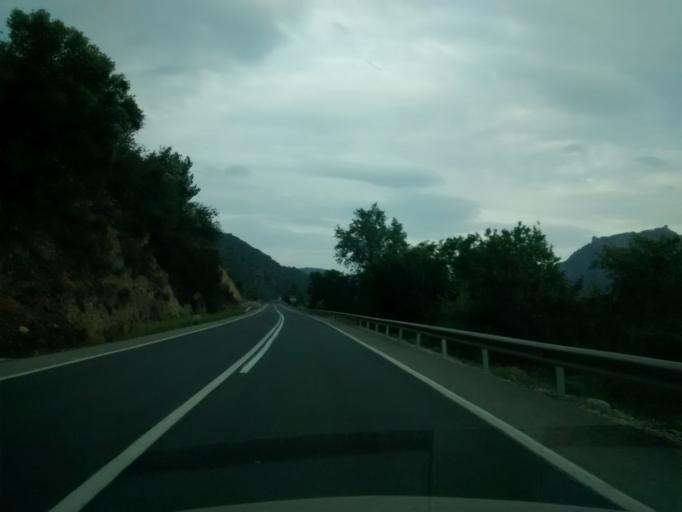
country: ES
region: Catalonia
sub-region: Provincia de Tarragona
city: Benifallet
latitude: 40.9754
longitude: 0.5130
